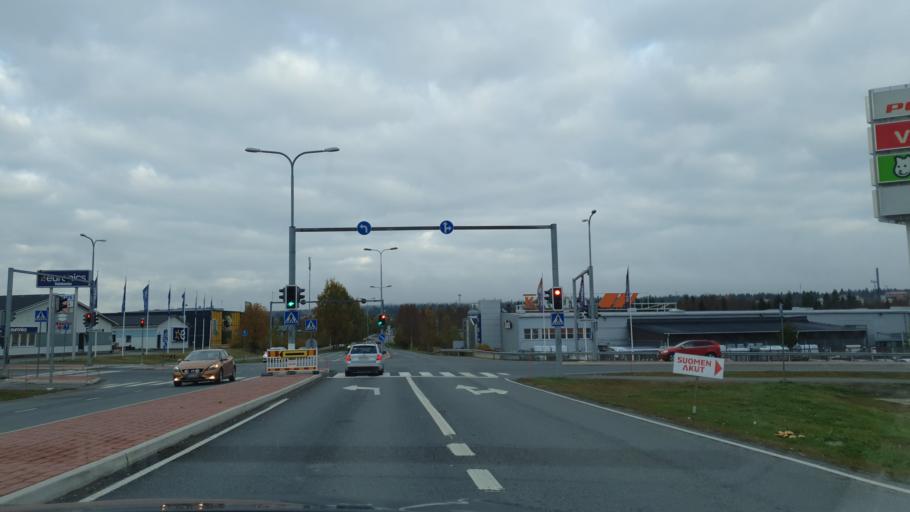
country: FI
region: Lapland
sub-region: Rovaniemi
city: Rovaniemi
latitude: 66.4929
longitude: 25.6920
